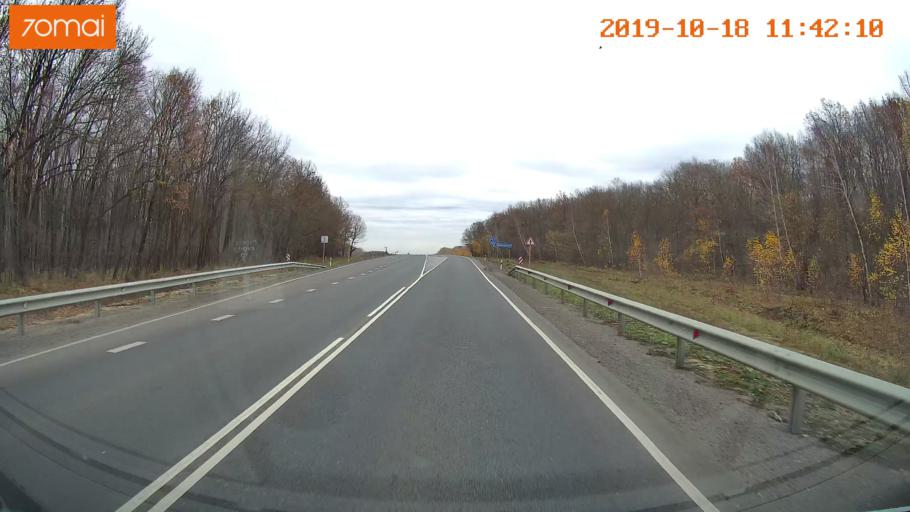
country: RU
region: Rjazan
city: Oktyabr'skiy
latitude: 54.1855
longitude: 38.9223
